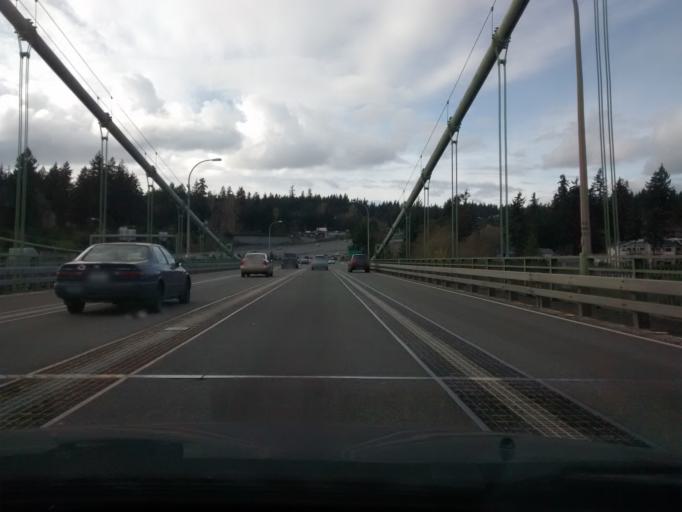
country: US
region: Washington
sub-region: Pierce County
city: Wollochet
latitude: 47.2730
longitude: -122.5562
